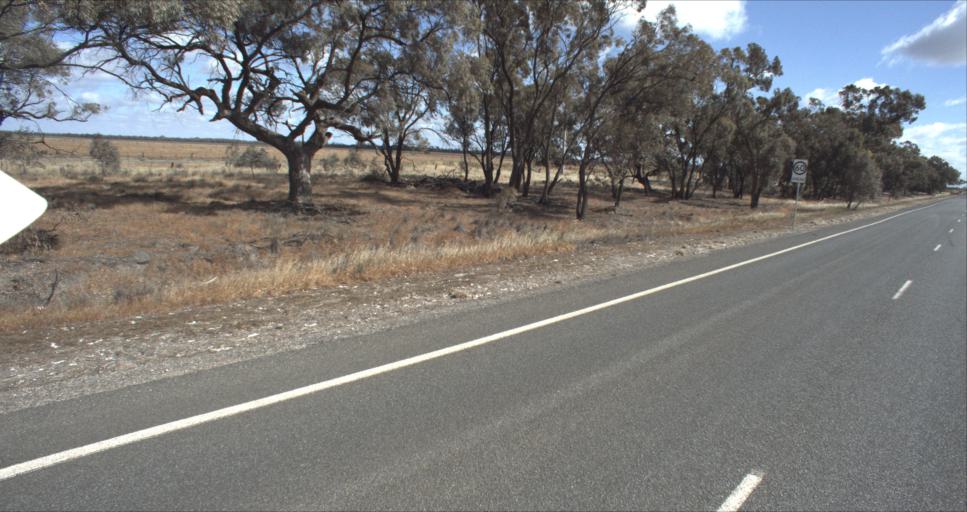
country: AU
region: New South Wales
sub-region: Murrumbidgee Shire
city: Darlington Point
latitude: -34.5581
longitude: 146.1695
